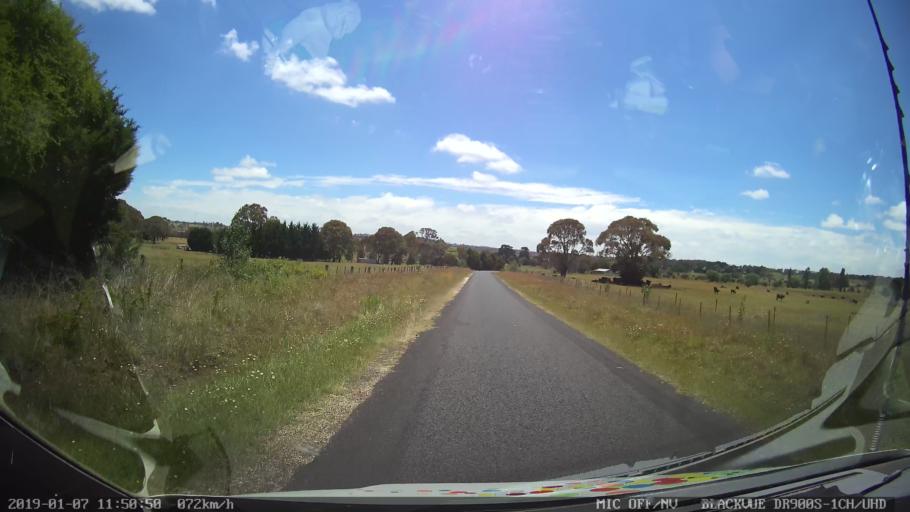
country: AU
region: New South Wales
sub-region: Guyra
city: Guyra
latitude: -30.3106
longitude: 151.6400
